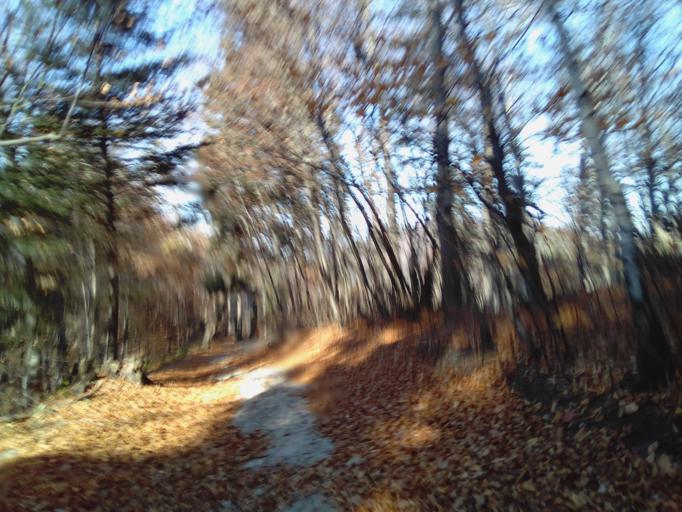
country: PL
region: Subcarpathian Voivodeship
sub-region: Powiat krosnienski
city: Leki
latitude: 49.8227
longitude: 21.6959
